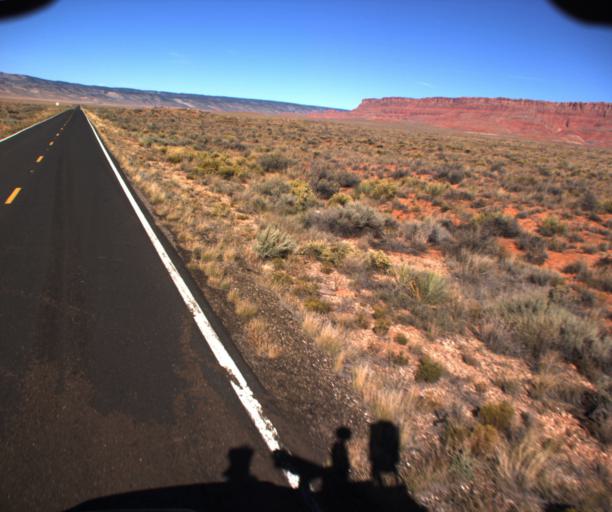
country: US
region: Arizona
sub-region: Coconino County
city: Page
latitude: 36.7008
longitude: -111.9295
